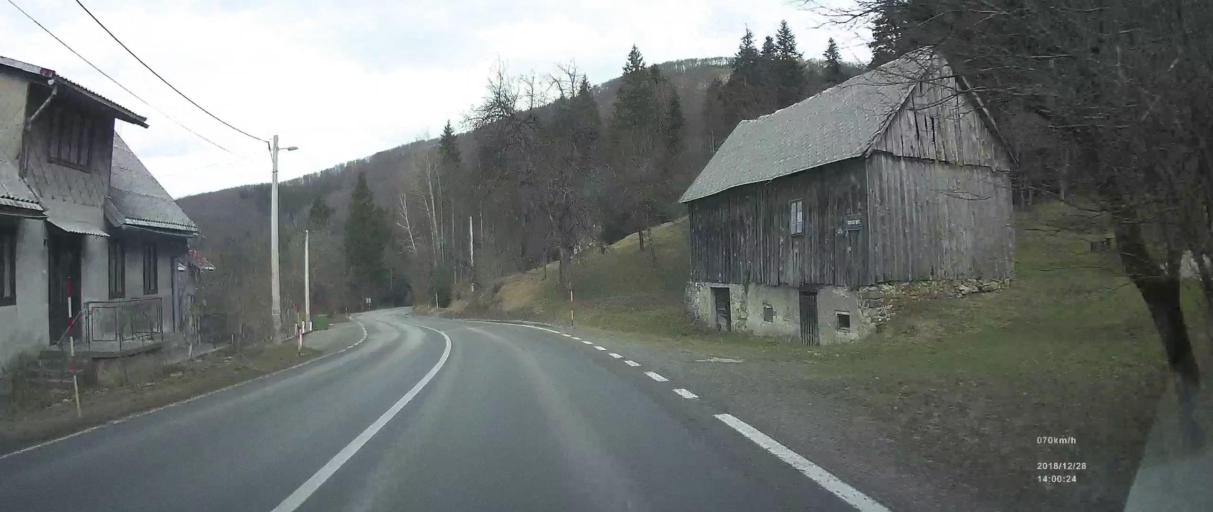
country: SI
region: Kostel
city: Kostel
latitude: 45.4116
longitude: 14.9136
